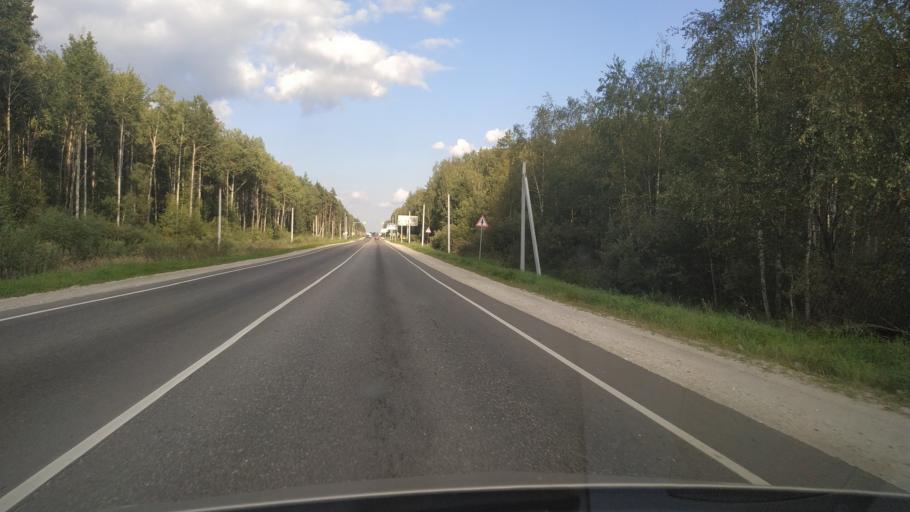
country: RU
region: Moskovskaya
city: Shaturtorf
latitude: 55.5780
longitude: 39.4336
